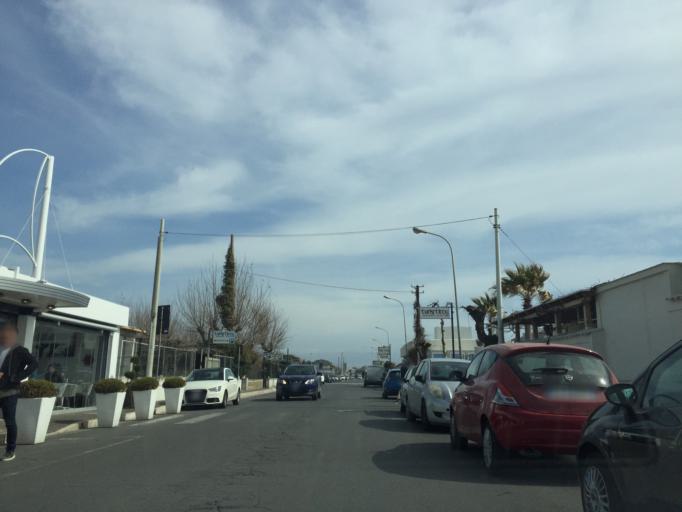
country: IT
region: Campania
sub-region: Provincia di Napoli
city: Bacoli
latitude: 40.7888
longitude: 14.0713
